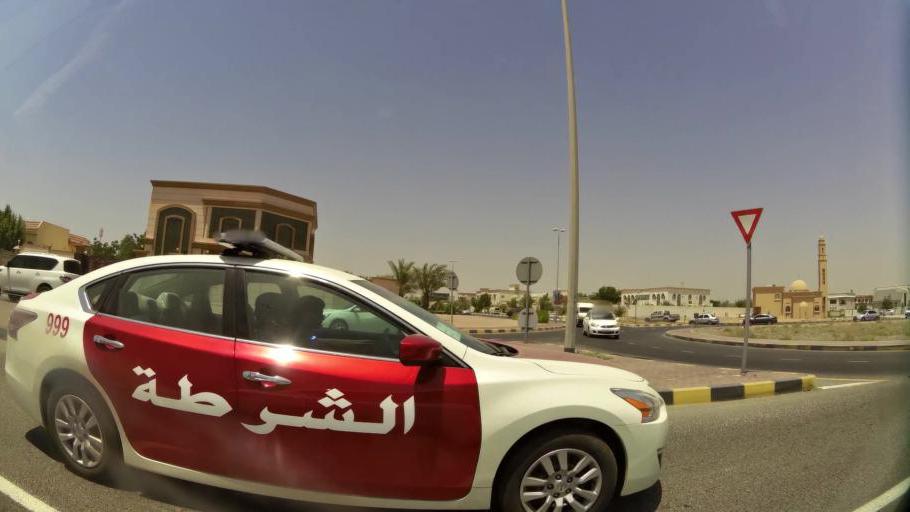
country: AE
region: Ajman
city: Ajman
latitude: 25.4191
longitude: 55.5137
